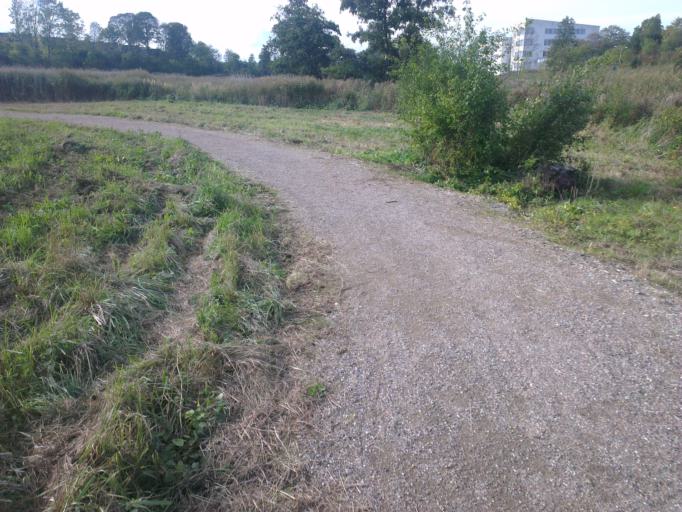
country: DK
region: Capital Region
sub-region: Frederikssund Kommune
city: Frederikssund
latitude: 55.8368
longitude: 12.0728
